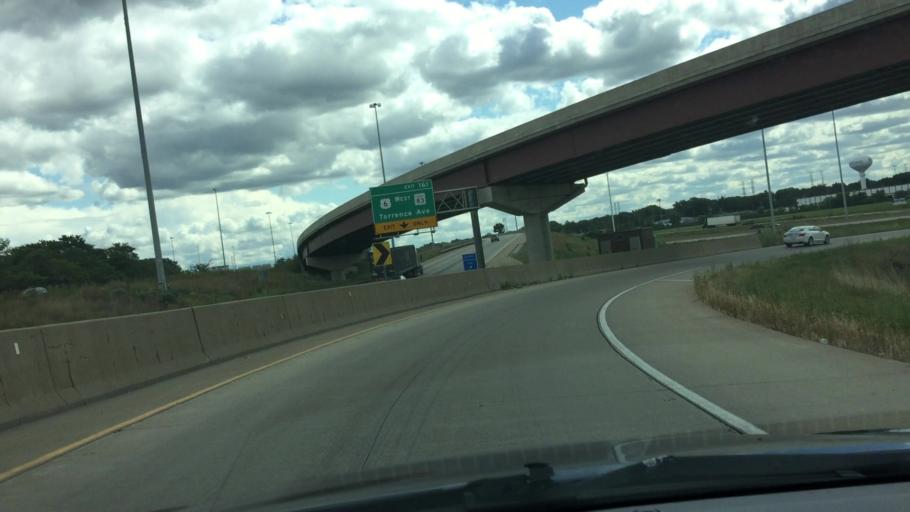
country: US
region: Illinois
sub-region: Cook County
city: Thornton
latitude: 41.5796
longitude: -87.5794
